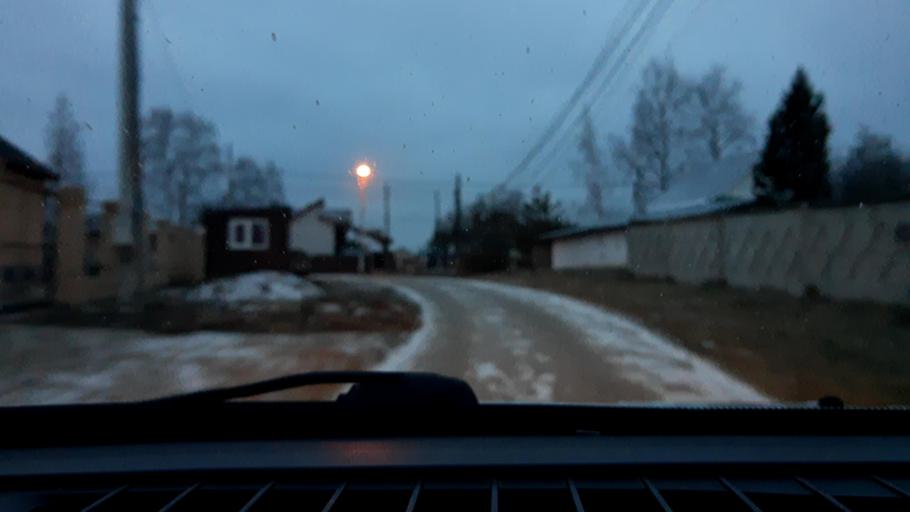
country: RU
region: Nizjnij Novgorod
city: Gorbatovka
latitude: 56.3867
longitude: 43.7517
